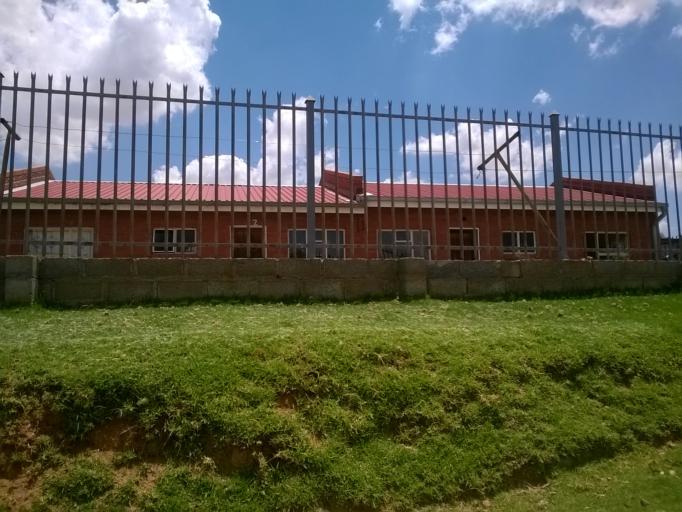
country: LS
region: Berea
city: Teyateyaneng
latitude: -29.1490
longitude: 27.7559
